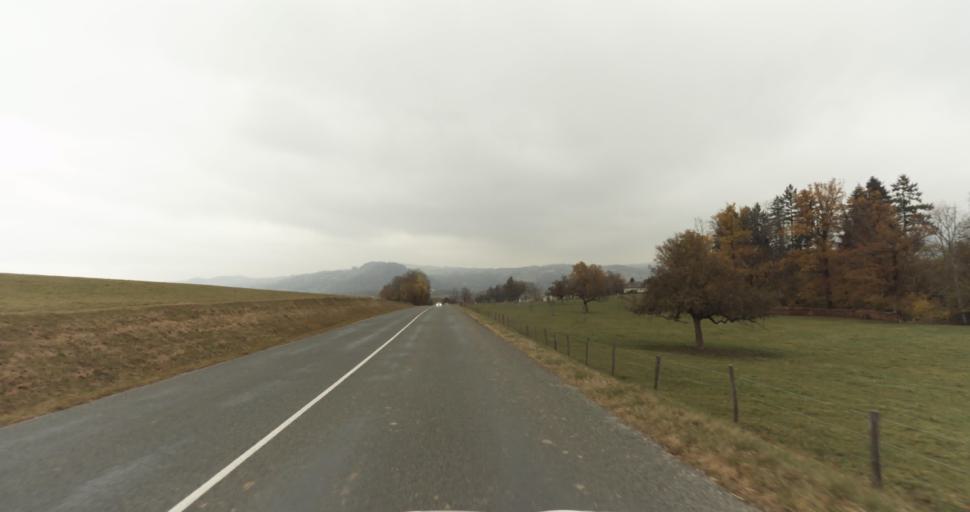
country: FR
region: Rhone-Alpes
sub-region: Departement de la Haute-Savoie
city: Alby-sur-Cheran
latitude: 45.8060
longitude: 6.0117
